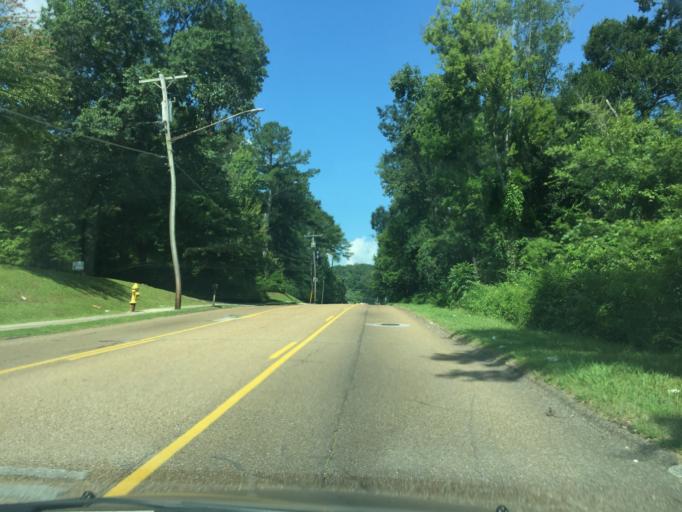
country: US
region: Tennessee
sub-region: Hamilton County
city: East Chattanooga
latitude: 35.0436
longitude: -85.2270
